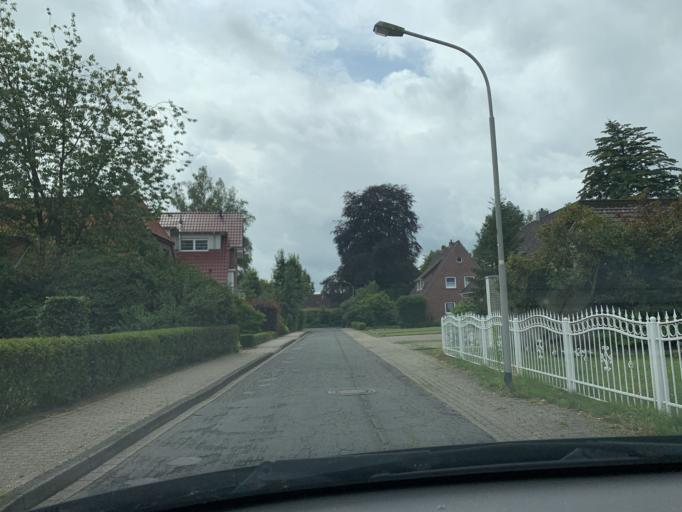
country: DE
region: Lower Saxony
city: Westerstede
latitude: 53.2523
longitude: 7.9217
